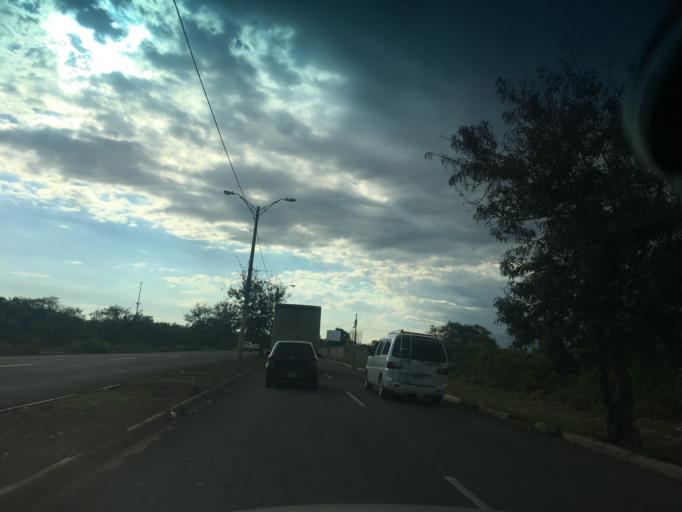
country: DO
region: La Romana
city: La Romana
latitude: 18.4204
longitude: -68.9861
